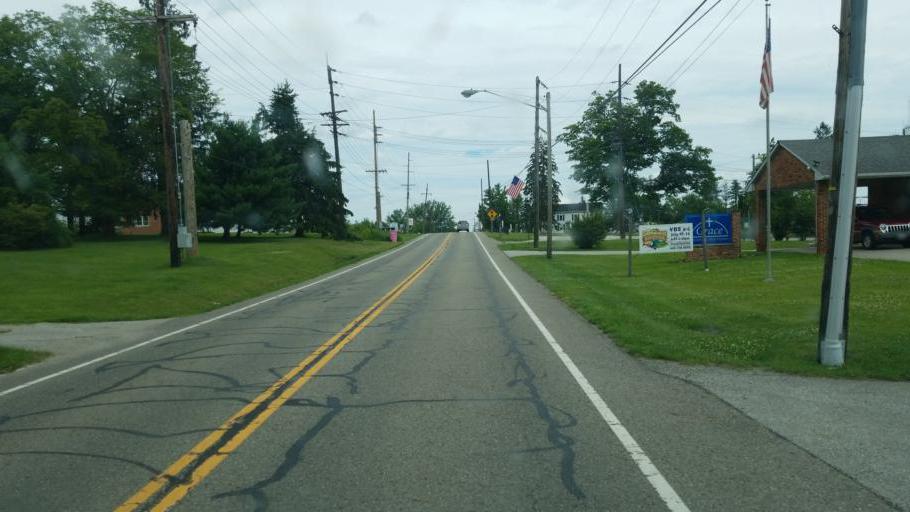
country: US
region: Ohio
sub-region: Geauga County
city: Burton
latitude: 41.4604
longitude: -81.2444
